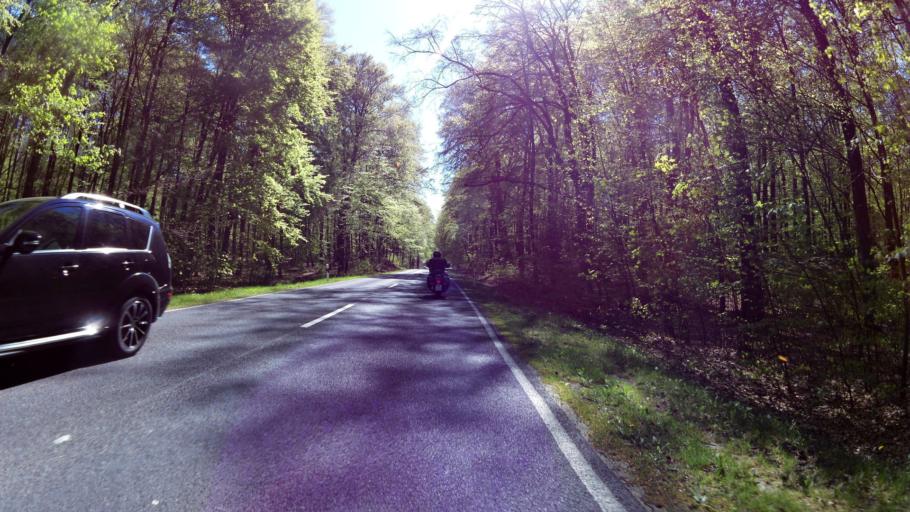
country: DE
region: Brandenburg
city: Wandlitz
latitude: 52.7255
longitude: 13.5103
